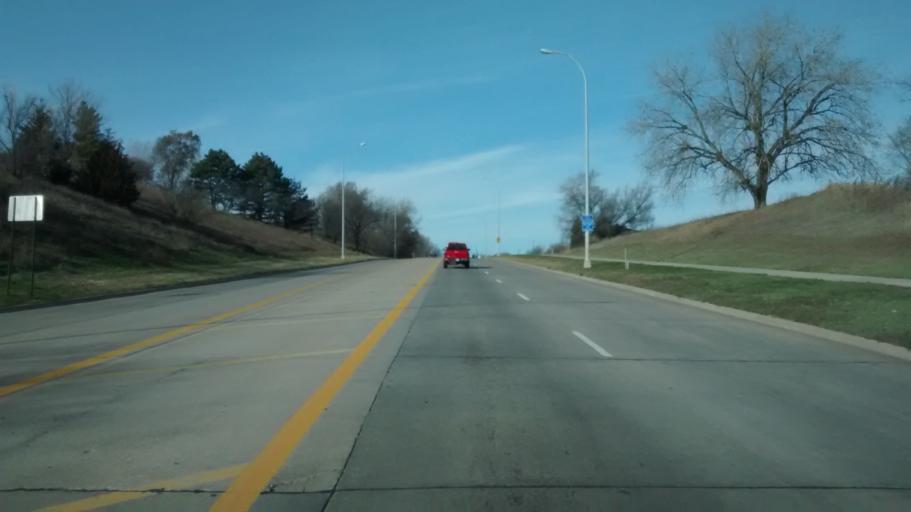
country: US
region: Iowa
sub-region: Woodbury County
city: Sioux City
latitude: 42.5347
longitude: -96.3712
